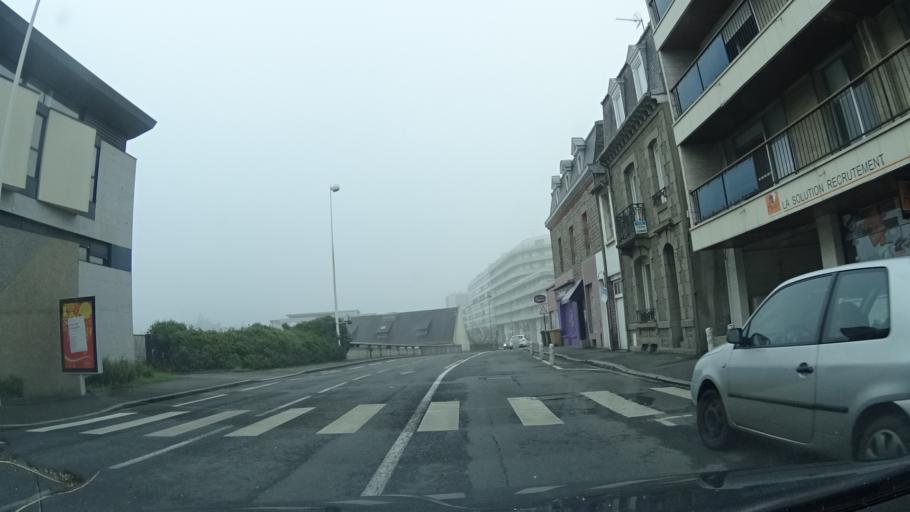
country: FR
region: Brittany
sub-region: Departement des Cotes-d'Armor
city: Saint-Brieuc
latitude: 48.5110
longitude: -2.7560
